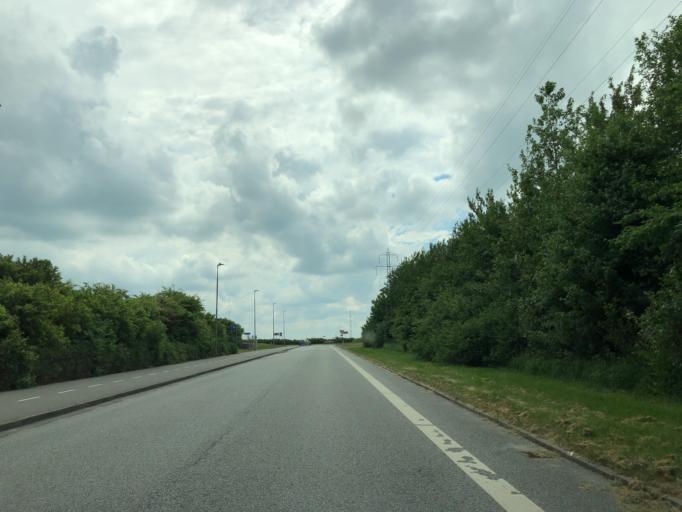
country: DK
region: Central Jutland
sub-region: Struer Kommune
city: Struer
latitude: 56.4751
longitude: 8.5910
